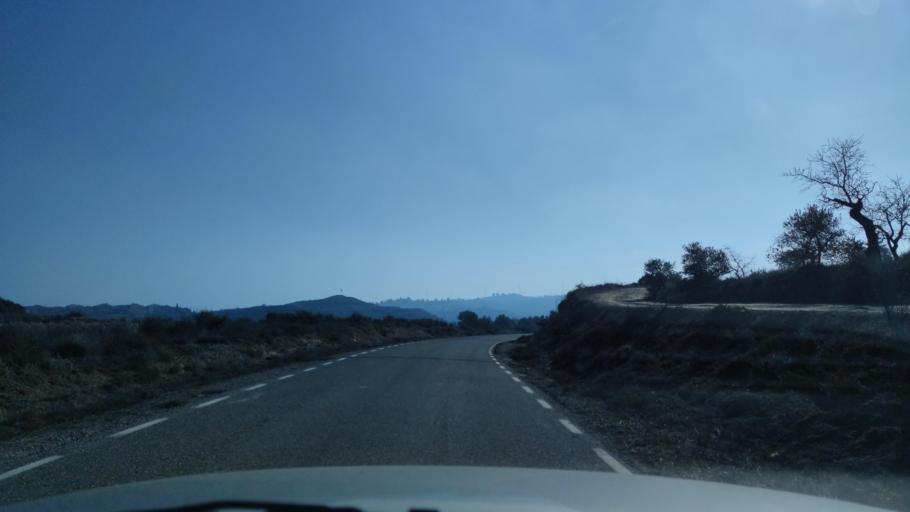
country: ES
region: Catalonia
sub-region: Provincia de Lleida
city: Torrebesses
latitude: 41.4290
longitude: 0.5845
